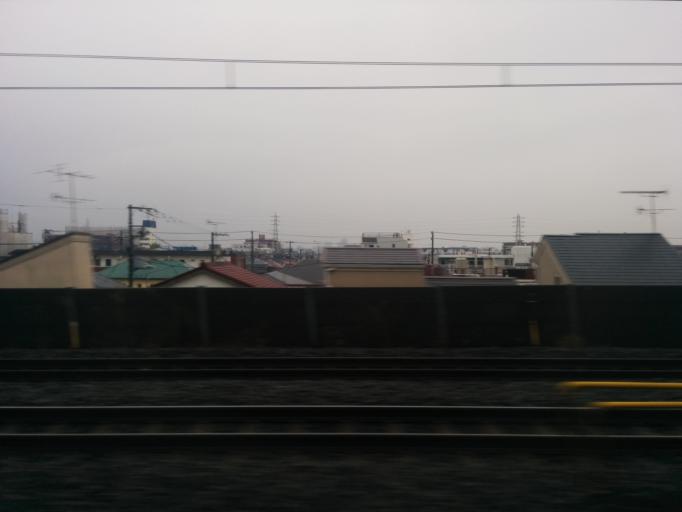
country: JP
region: Chiba
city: Matsudo
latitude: 35.7260
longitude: 139.9151
